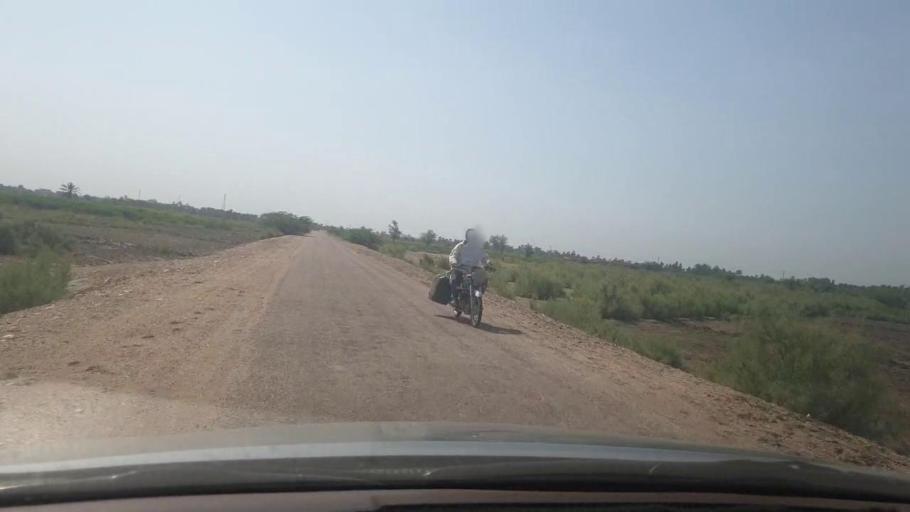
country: PK
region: Sindh
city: Ranipur
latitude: 27.2631
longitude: 68.5831
